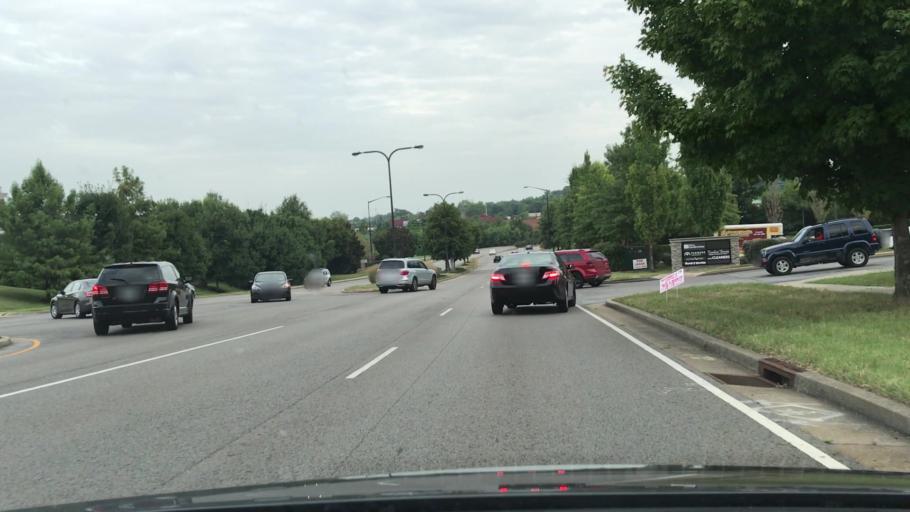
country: US
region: Tennessee
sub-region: Williamson County
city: Brentwood Estates
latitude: 35.9596
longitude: -86.8018
